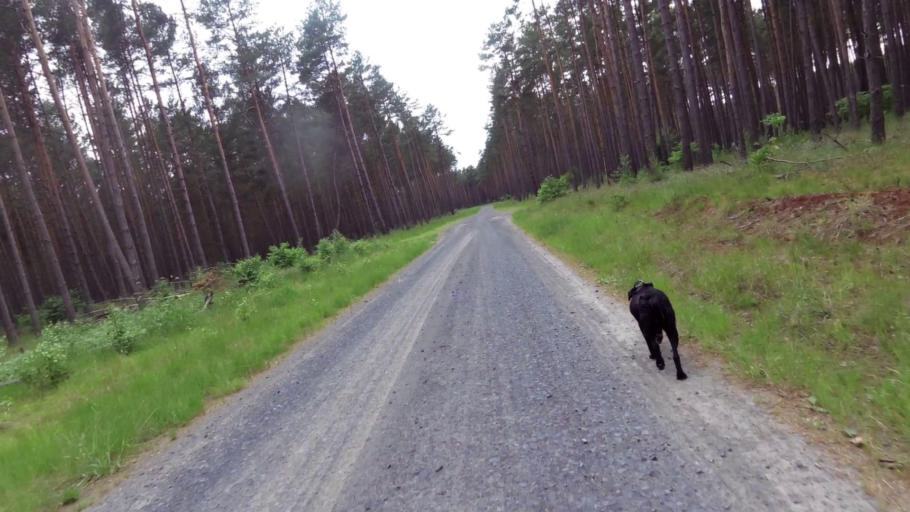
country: PL
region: West Pomeranian Voivodeship
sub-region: Powiat mysliborski
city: Debno
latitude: 52.8313
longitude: 14.6364
